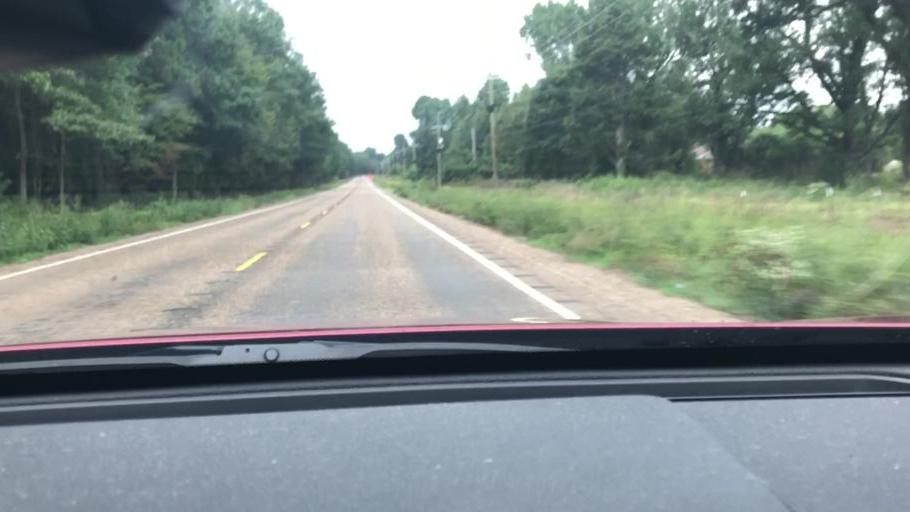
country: US
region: Texas
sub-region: Bowie County
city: Wake Village
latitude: 33.3787
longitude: -94.1022
